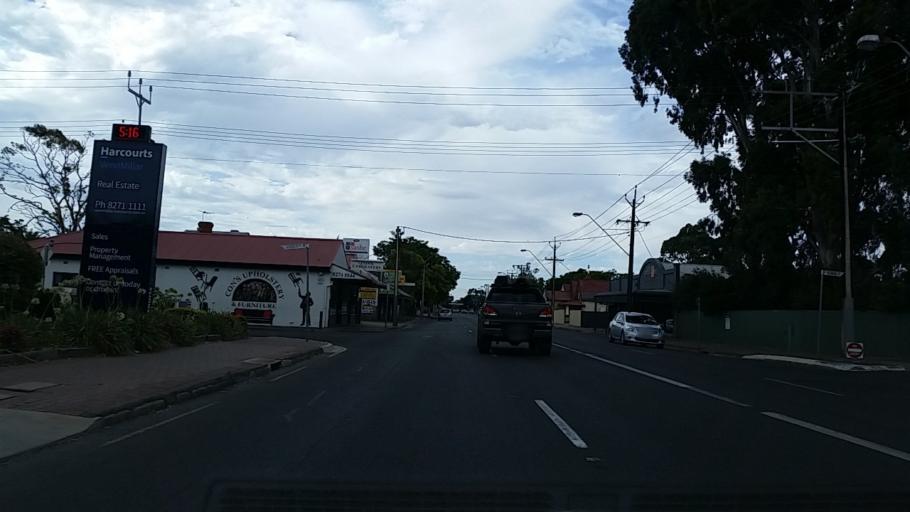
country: AU
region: South Australia
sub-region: Mitcham
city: Clarence Gardens
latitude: -34.9713
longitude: 138.5911
